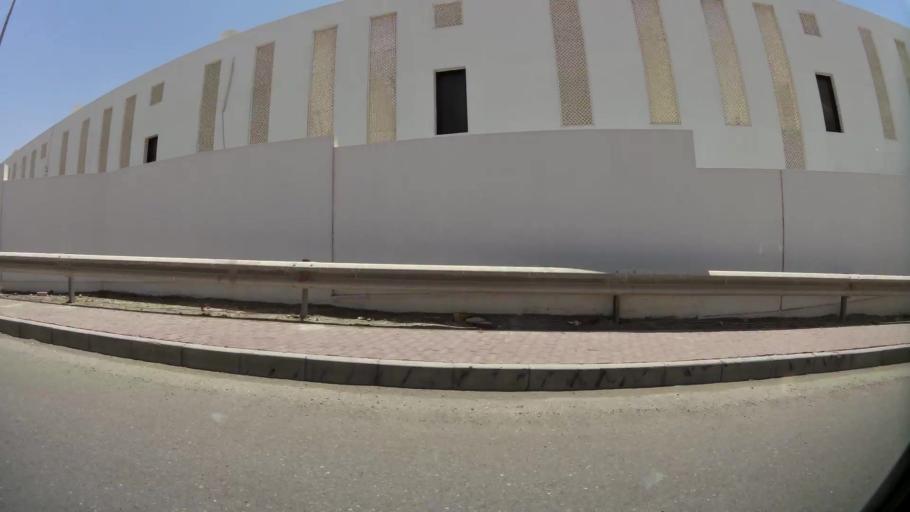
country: OM
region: Muhafazat Masqat
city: Muscat
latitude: 23.6243
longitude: 58.4917
